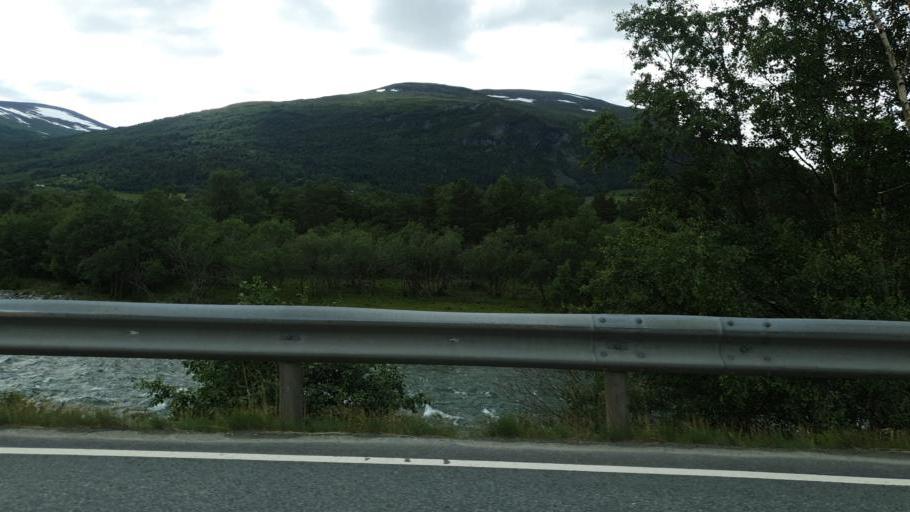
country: NO
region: Sor-Trondelag
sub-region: Oppdal
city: Oppdal
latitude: 62.5512
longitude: 9.6325
